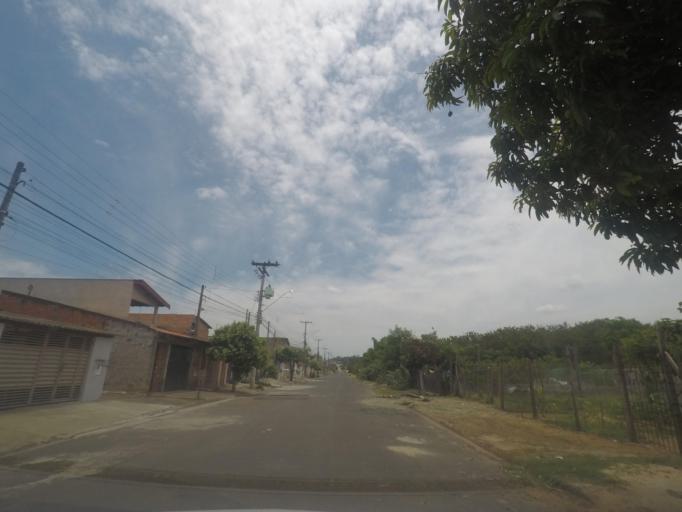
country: BR
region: Sao Paulo
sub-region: Nova Odessa
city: Nova Odessa
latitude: -22.7901
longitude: -47.2766
